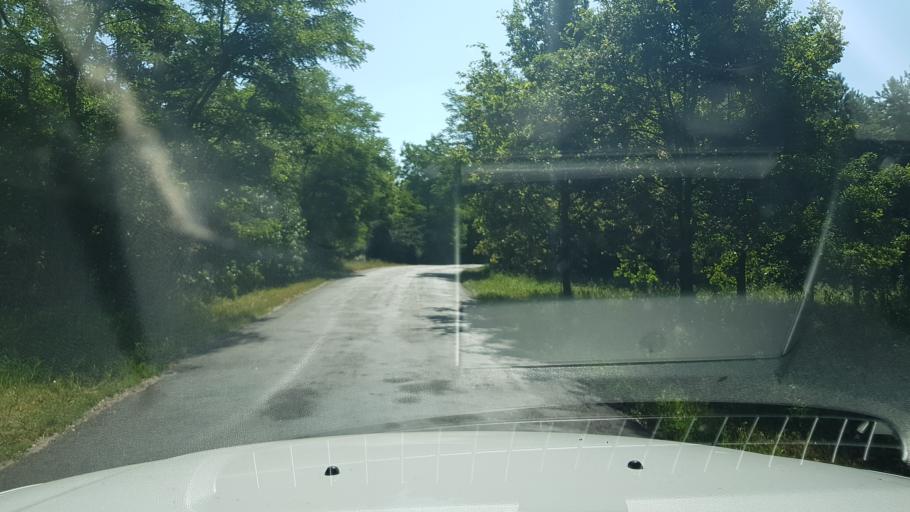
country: PL
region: West Pomeranian Voivodeship
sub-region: Powiat goleniowski
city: Goleniow
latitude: 53.4737
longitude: 14.7147
